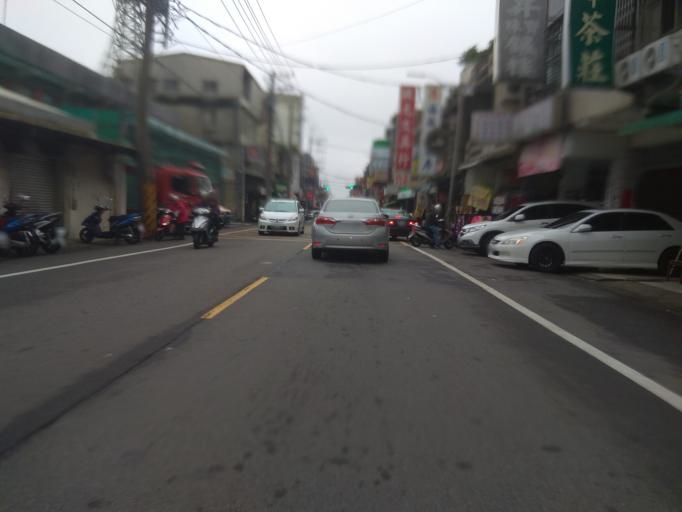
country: TW
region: Taiwan
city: Taoyuan City
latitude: 25.0126
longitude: 121.1366
